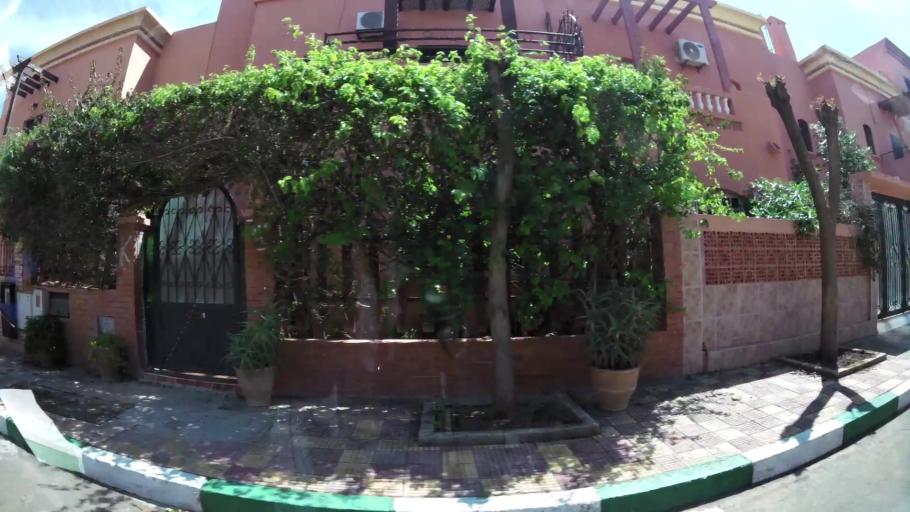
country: MA
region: Marrakech-Tensift-Al Haouz
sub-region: Marrakech
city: Marrakesh
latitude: 31.6489
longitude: -8.0610
